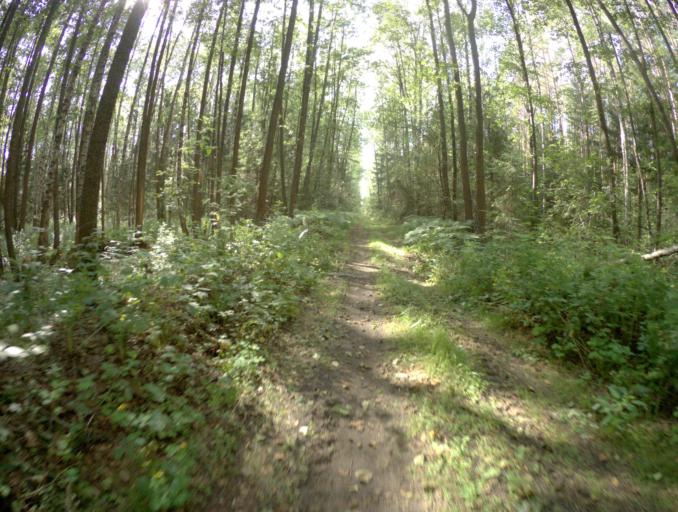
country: RU
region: Vladimir
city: Sobinka
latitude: 55.9174
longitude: 40.0873
